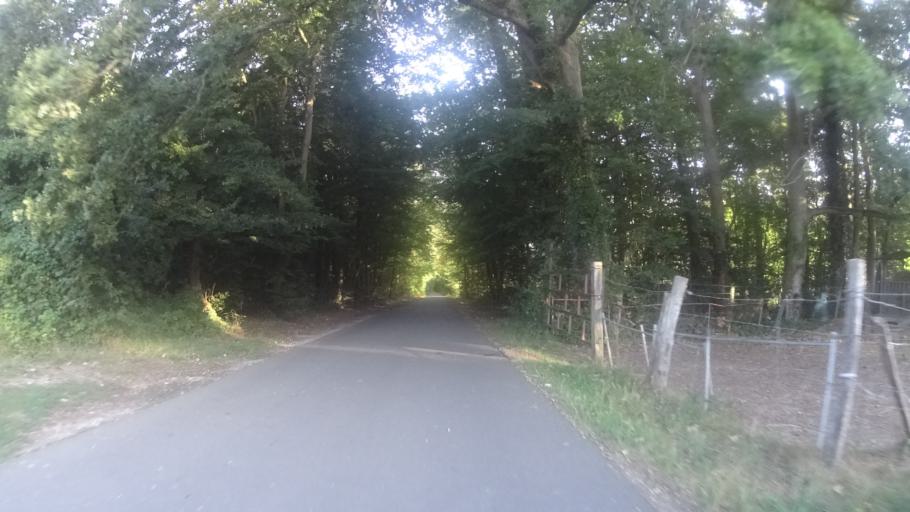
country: FR
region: Picardie
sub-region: Departement de l'Oise
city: Ver-sur-Launette
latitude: 49.1745
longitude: 2.6786
